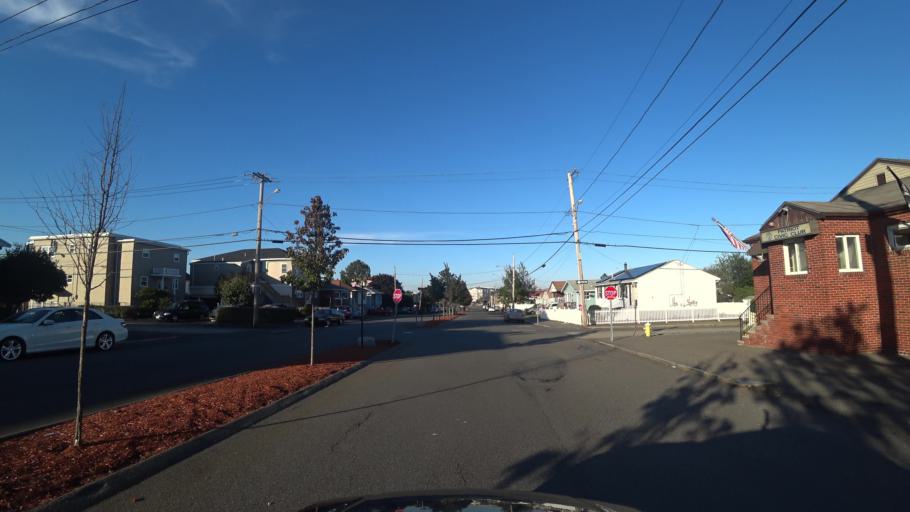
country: US
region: Massachusetts
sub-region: Suffolk County
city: Revere
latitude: 42.4209
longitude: -71.0102
